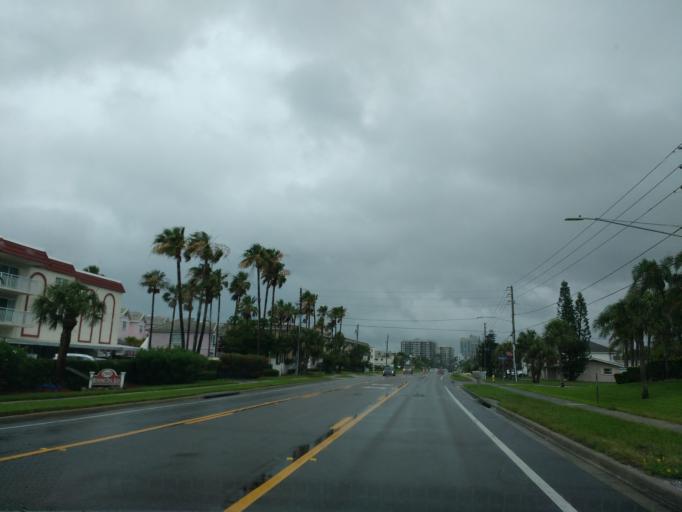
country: US
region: Florida
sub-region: Pinellas County
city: Belleair Beach
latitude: 27.9311
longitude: -82.8414
